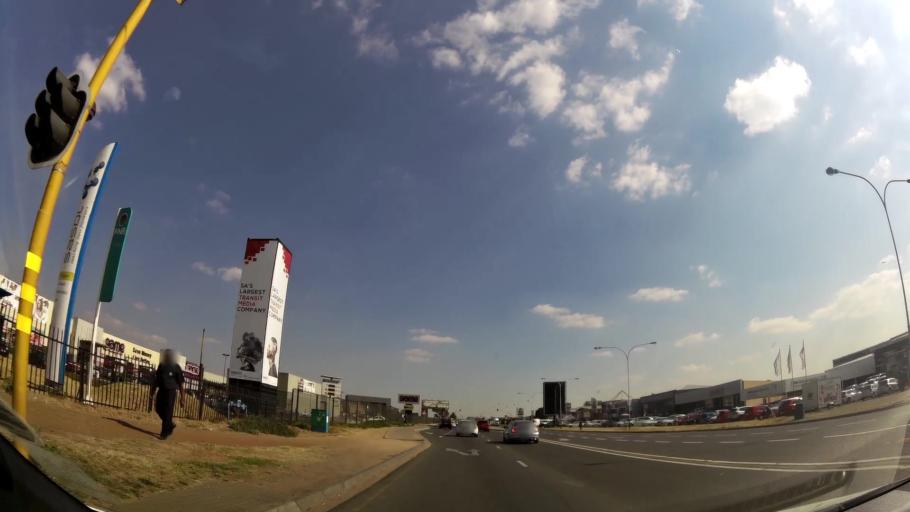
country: ZA
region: Gauteng
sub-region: Ekurhuleni Metropolitan Municipality
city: Boksburg
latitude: -26.1787
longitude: 28.2408
